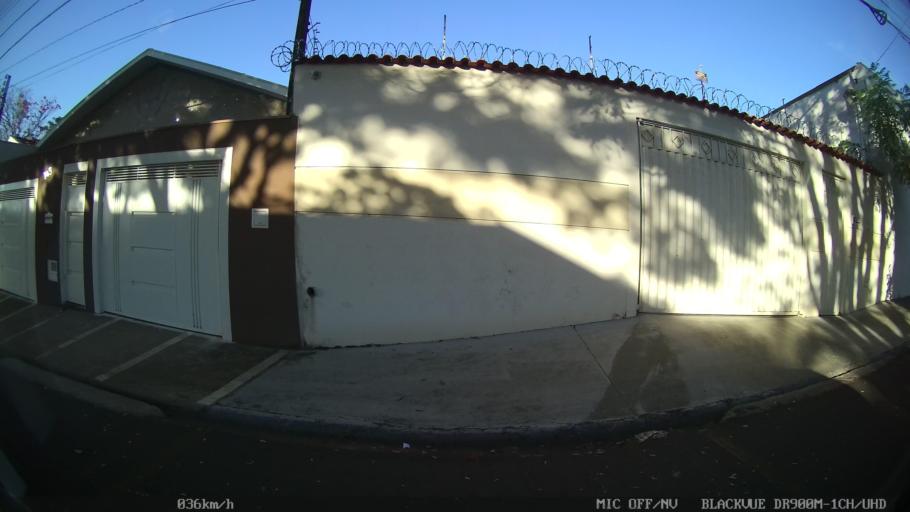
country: BR
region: Sao Paulo
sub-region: Franca
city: Franca
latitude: -20.5243
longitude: -47.3779
